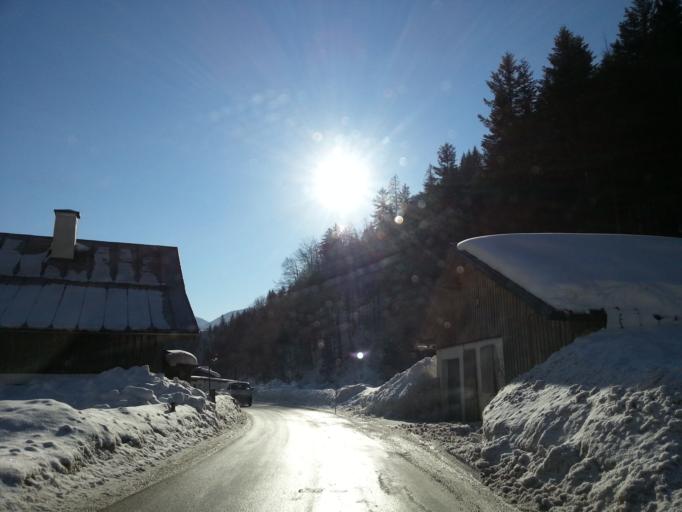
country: AT
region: Salzburg
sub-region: Politischer Bezirk Hallein
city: Abtenau
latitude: 47.4946
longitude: 13.3941
